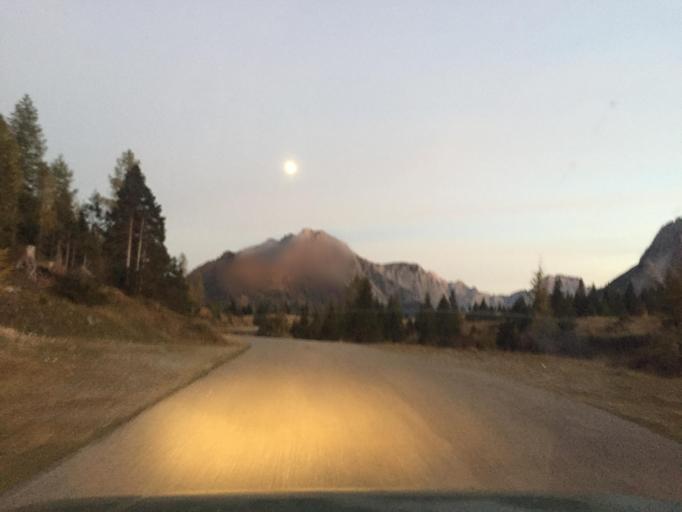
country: IT
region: Veneto
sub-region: Provincia di Belluno
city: Granvilla
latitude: 46.6230
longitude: 12.7112
